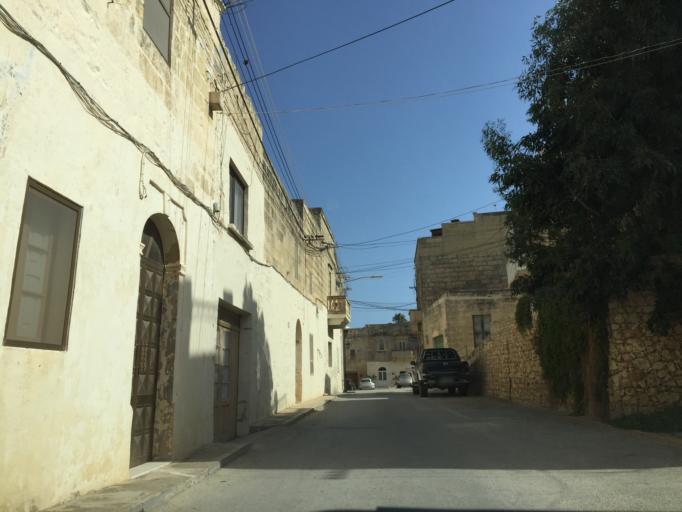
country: MT
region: L-Gharb
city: Gharb
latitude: 36.0629
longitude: 14.2091
